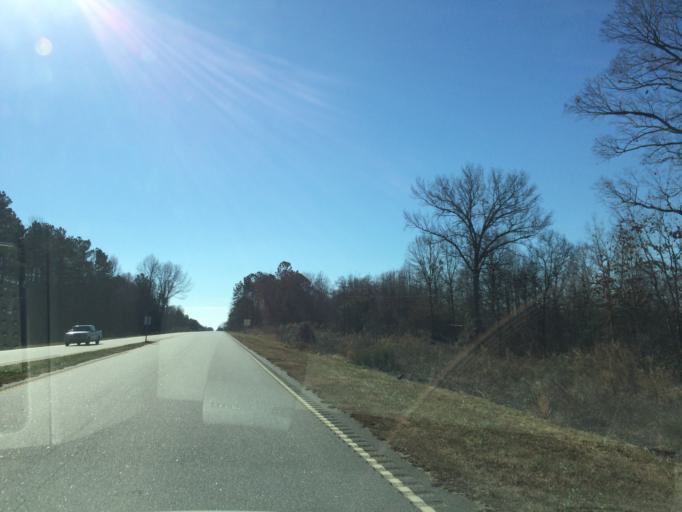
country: US
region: South Carolina
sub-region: Anderson County
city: Williamston
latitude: 34.6272
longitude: -82.5322
